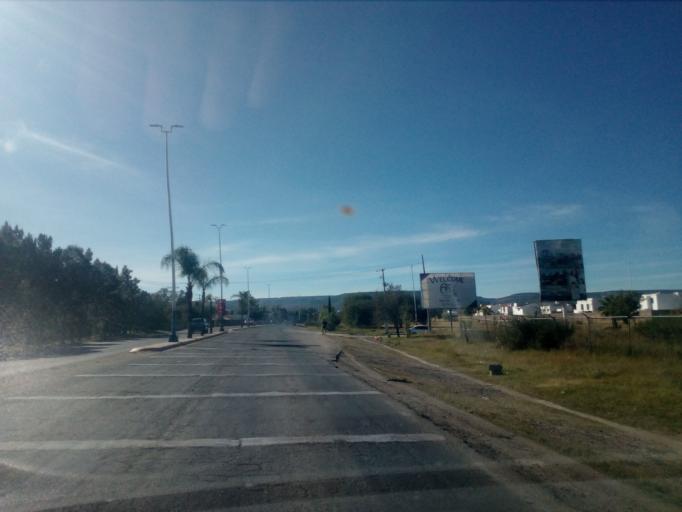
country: MX
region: Durango
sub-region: Durango
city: Sebastian Lerdo de Tejada
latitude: 23.9784
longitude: -104.6643
